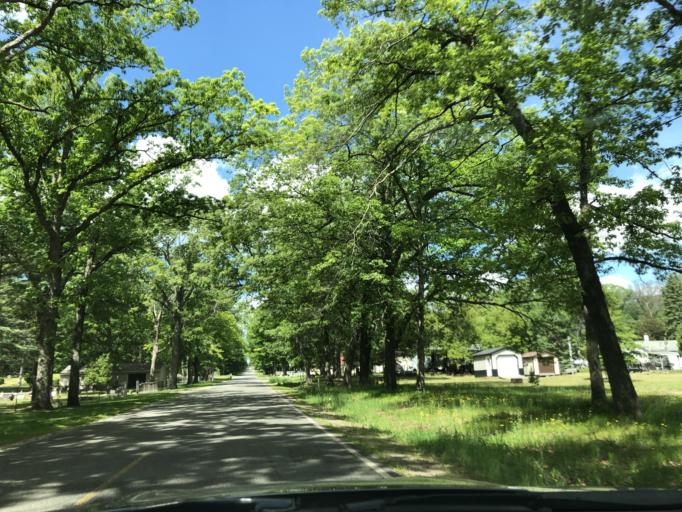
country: US
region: Michigan
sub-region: Clare County
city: Harrison
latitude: 44.0315
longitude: -84.8091
